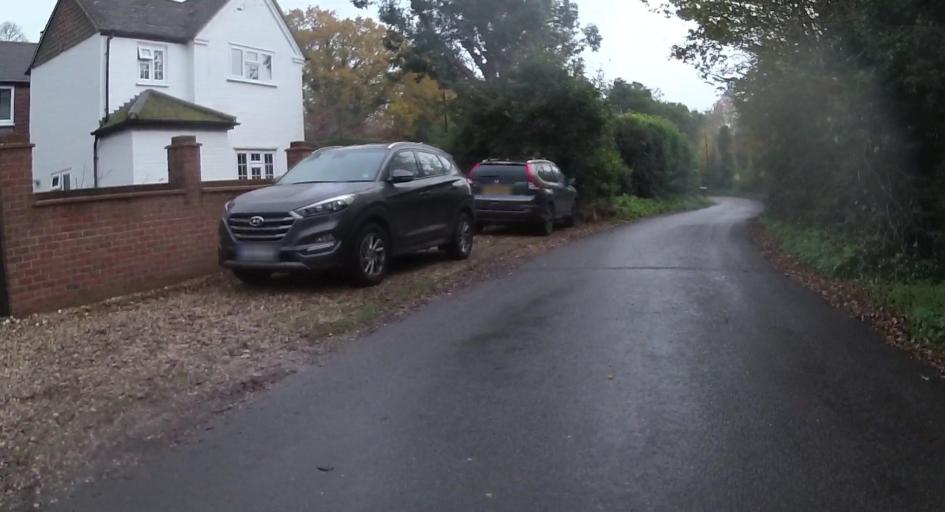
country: GB
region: England
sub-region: Wokingham
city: Finchampstead
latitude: 51.3658
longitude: -0.8568
